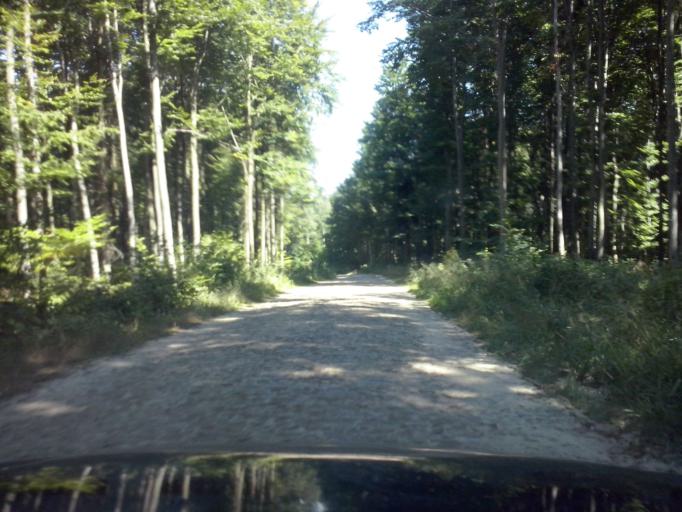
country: PL
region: Swietokrzyskie
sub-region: Powiat kielecki
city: Bieliny
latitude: 50.7891
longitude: 20.9345
